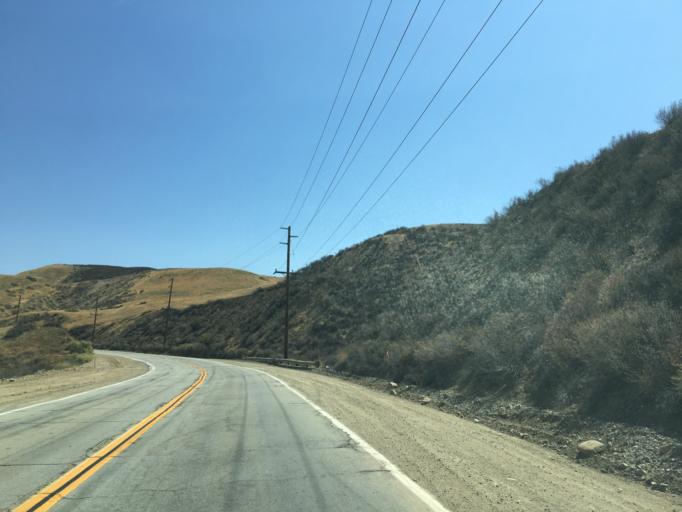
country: US
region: California
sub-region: Los Angeles County
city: Castaic
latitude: 34.5008
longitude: -118.6050
